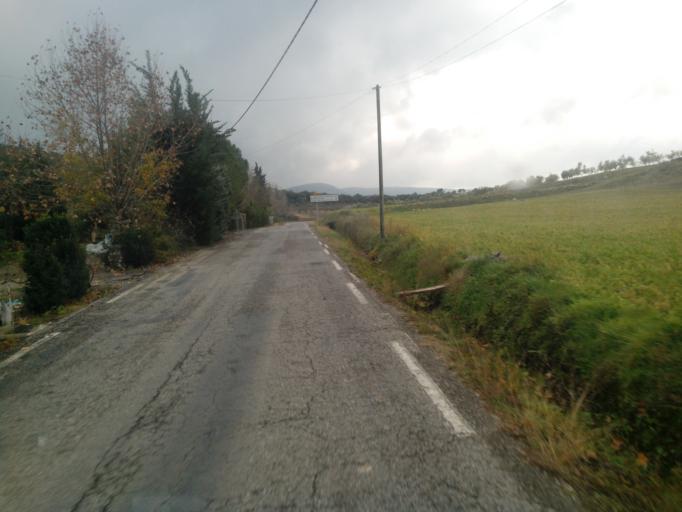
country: FR
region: Languedoc-Roussillon
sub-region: Departement du Gard
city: Saint-Hippolyte-du-Fort
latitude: 43.9539
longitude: 3.8094
